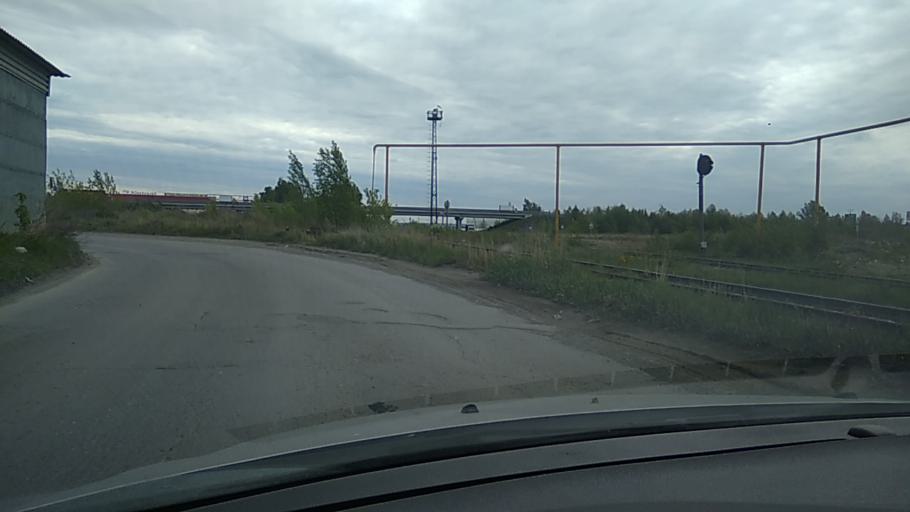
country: RU
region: Sverdlovsk
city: Istok
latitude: 56.7539
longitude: 60.7528
